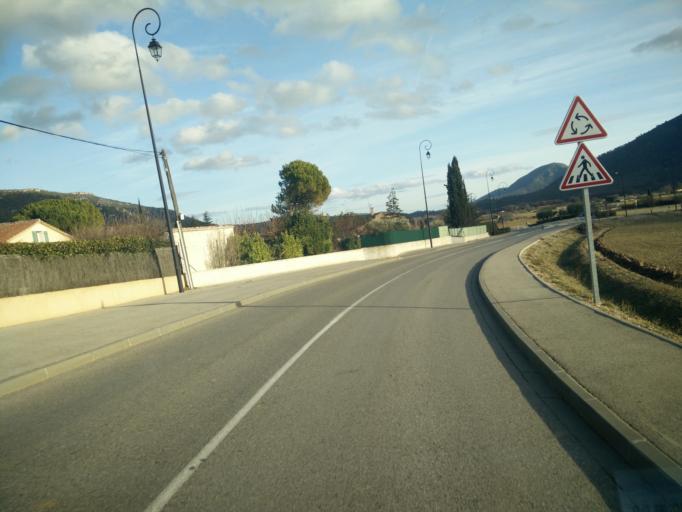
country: FR
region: Provence-Alpes-Cote d'Azur
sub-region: Departement du Var
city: Signes
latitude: 43.2902
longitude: 5.8698
